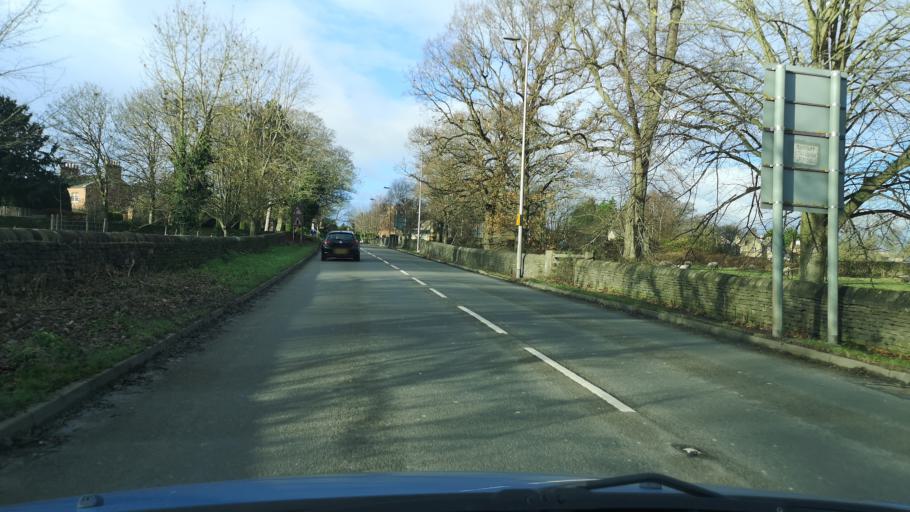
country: GB
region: England
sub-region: City and Borough of Wakefield
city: Crigglestone
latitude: 53.6169
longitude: -1.5648
